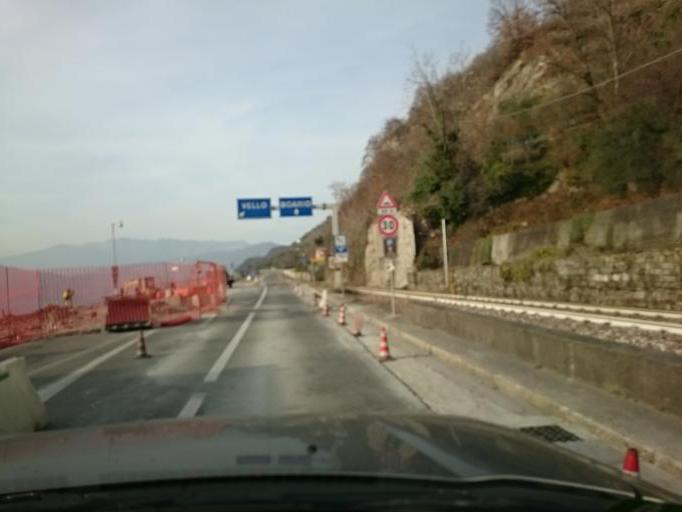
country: IT
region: Lombardy
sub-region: Provincia di Brescia
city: Marone
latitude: 45.7497
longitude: 10.0868
